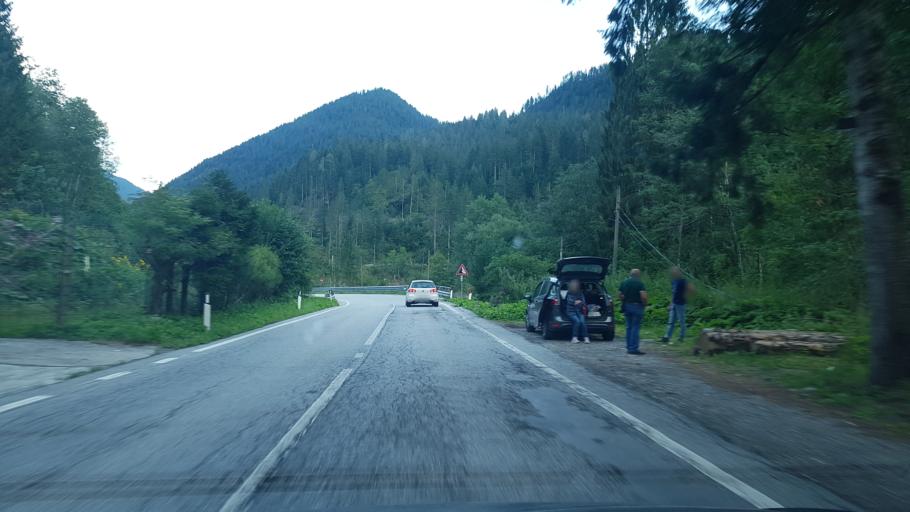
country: IT
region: Friuli Venezia Giulia
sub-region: Provincia di Udine
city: Forni Avoltri
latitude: 46.5733
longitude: 12.8002
